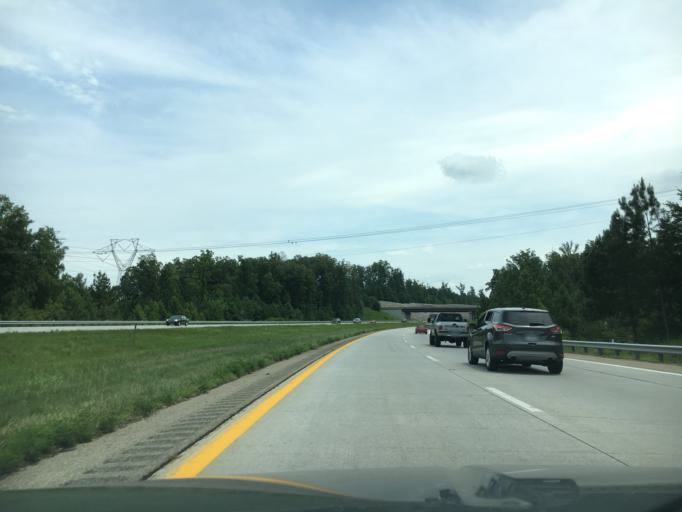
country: US
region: Virginia
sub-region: Chesterfield County
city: Brandermill
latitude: 37.4860
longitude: -77.6678
